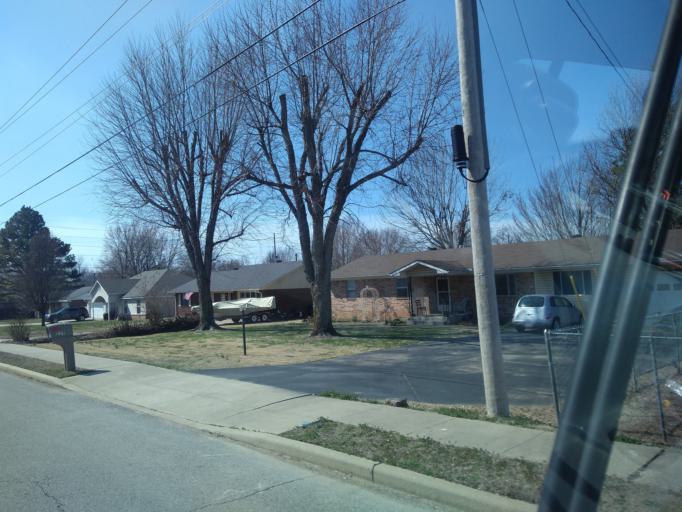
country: US
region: Arkansas
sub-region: Washington County
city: Farmington
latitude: 36.0513
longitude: -94.2360
